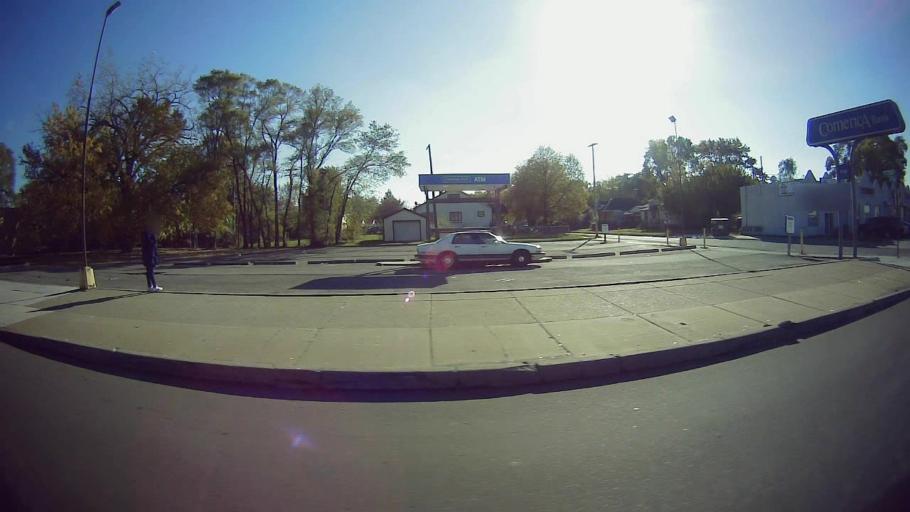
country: US
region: Michigan
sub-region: Wayne County
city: Highland Park
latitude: 42.4329
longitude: -83.0769
